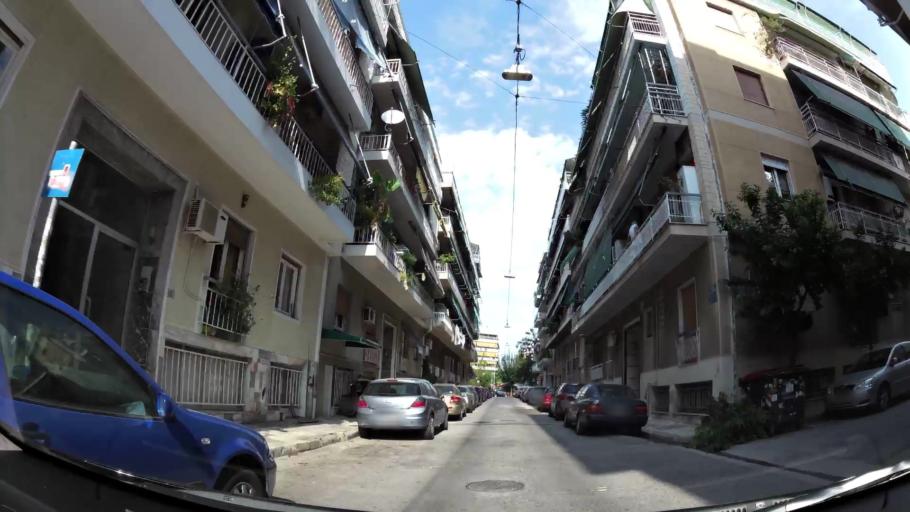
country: GR
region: Attica
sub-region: Nomarchia Athinas
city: Athens
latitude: 37.9914
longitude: 23.7182
